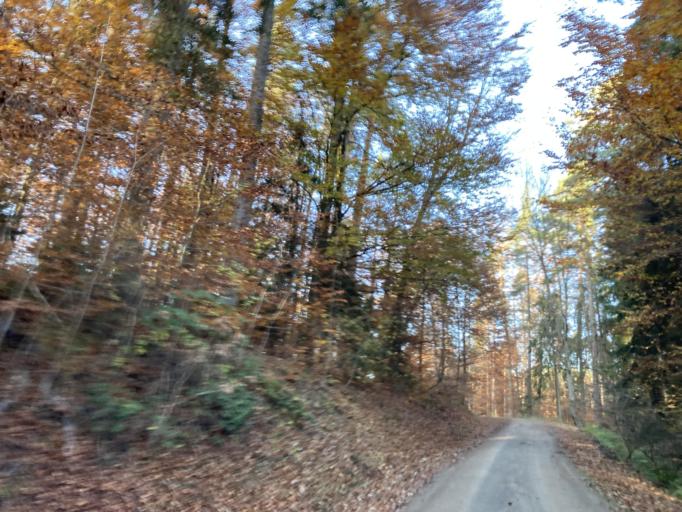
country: DE
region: Baden-Wuerttemberg
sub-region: Tuebingen Region
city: Tuebingen
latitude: 48.5403
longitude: 8.9979
